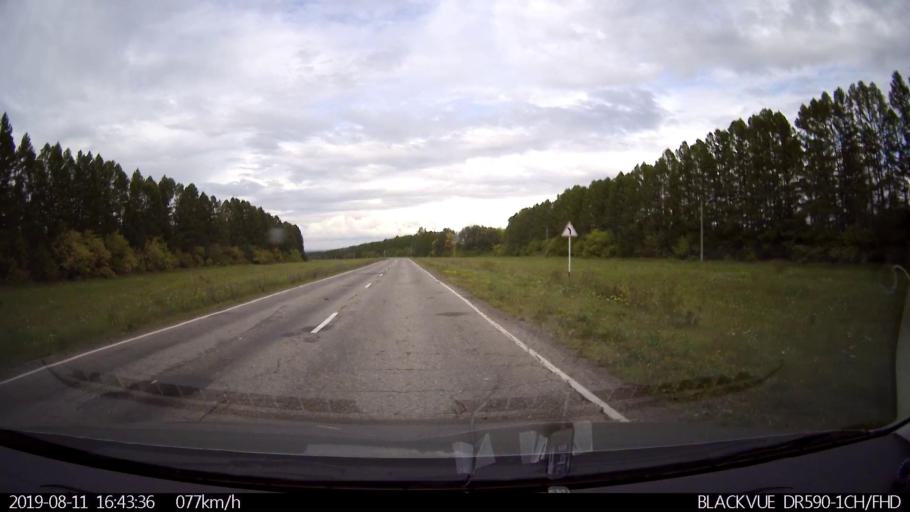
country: RU
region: Ulyanovsk
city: Mayna
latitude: 54.1706
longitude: 47.6739
